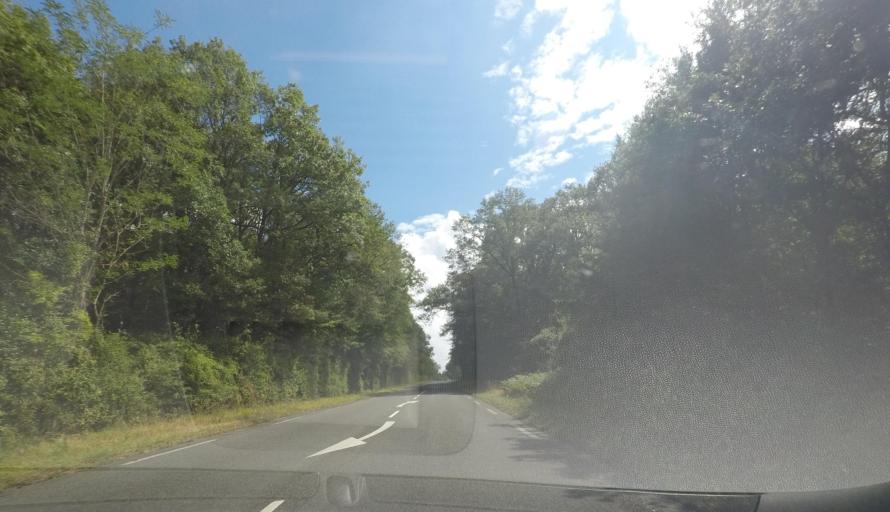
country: FR
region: Pays de la Loire
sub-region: Departement de la Sarthe
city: Saint-Cosme-en-Vairais
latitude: 48.2693
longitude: 0.4943
